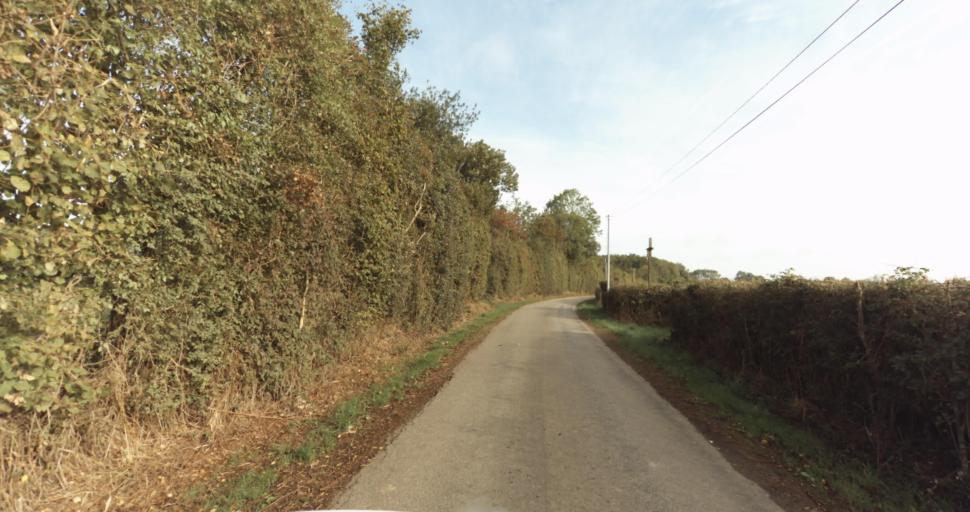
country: FR
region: Lower Normandy
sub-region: Departement de l'Orne
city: Vimoutiers
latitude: 48.9070
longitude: 0.2976
